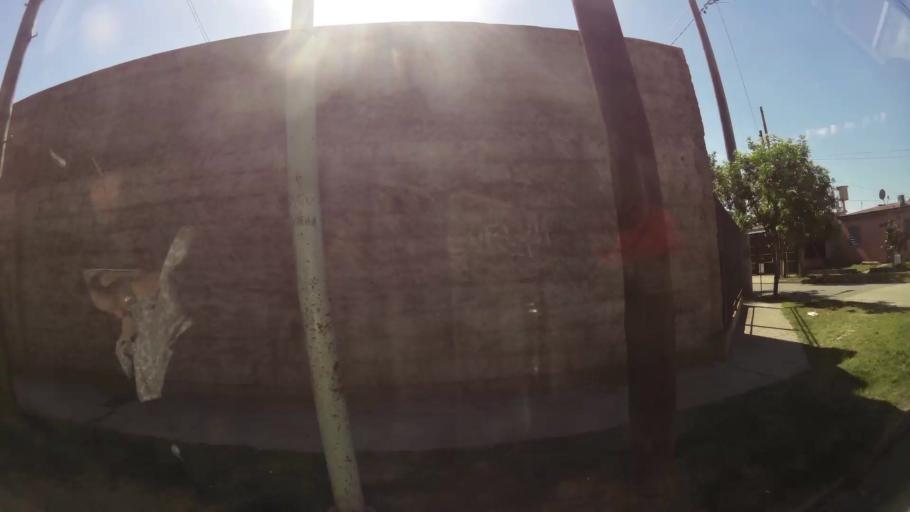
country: AR
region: Cordoba
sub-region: Departamento de Capital
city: Cordoba
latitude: -31.3637
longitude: -64.1527
